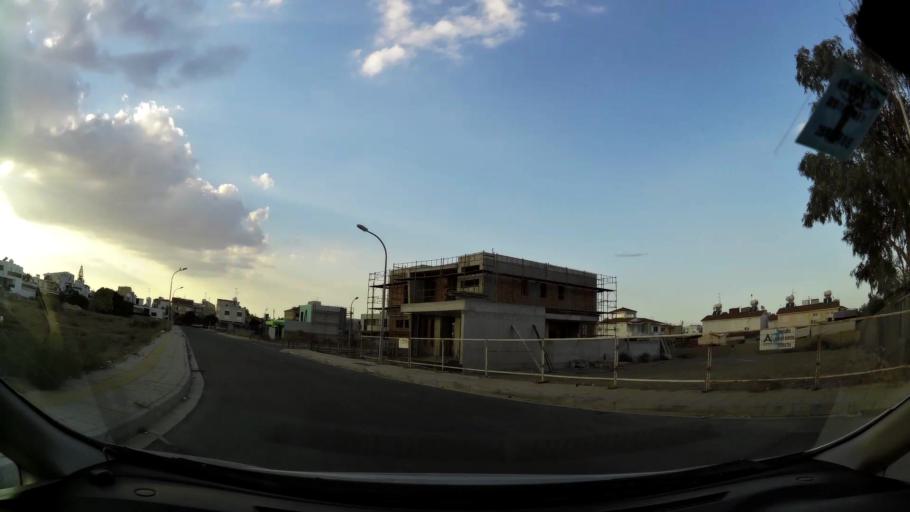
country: CY
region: Lefkosia
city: Tseri
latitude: 35.1261
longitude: 33.3299
